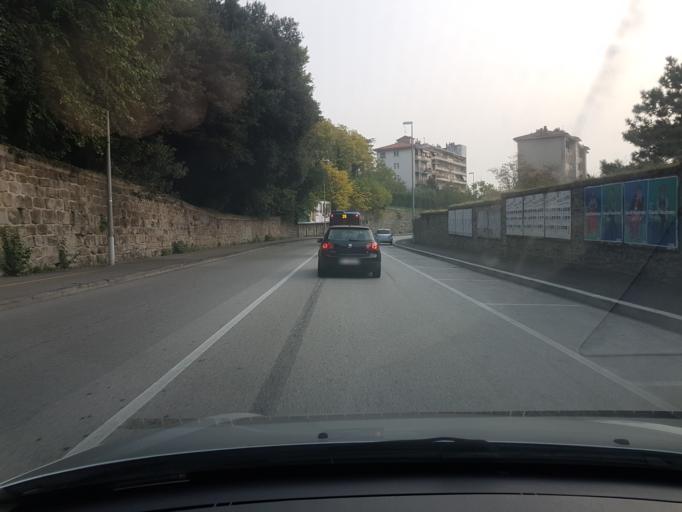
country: IT
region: Friuli Venezia Giulia
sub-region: Provincia di Trieste
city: Trieste
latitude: 45.6390
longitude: 13.7803
